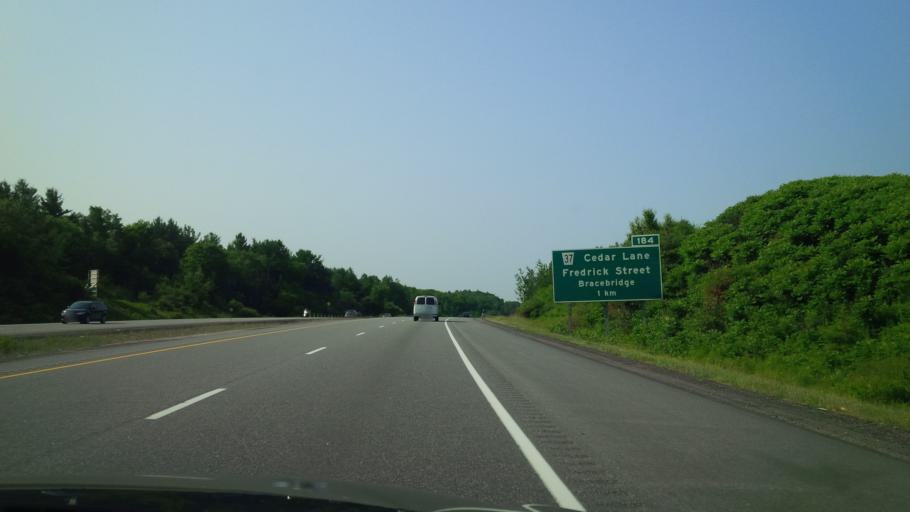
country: CA
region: Ontario
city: Bracebridge
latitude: 45.0251
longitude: -79.2923
